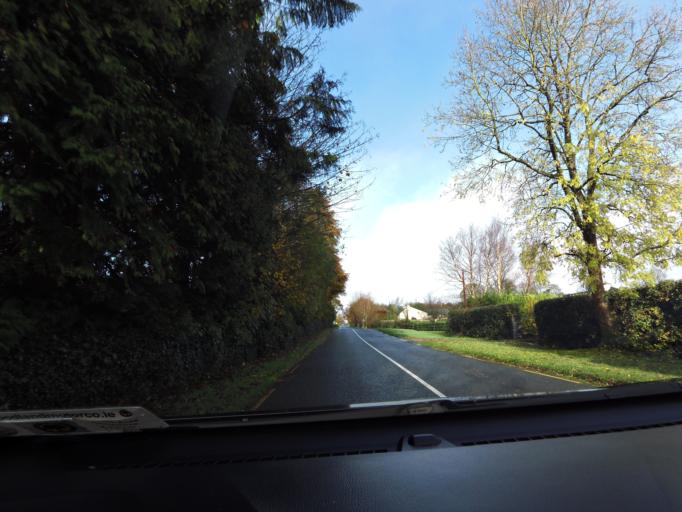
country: IE
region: Leinster
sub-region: An Iarmhi
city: Moate
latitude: 53.3782
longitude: -7.7989
